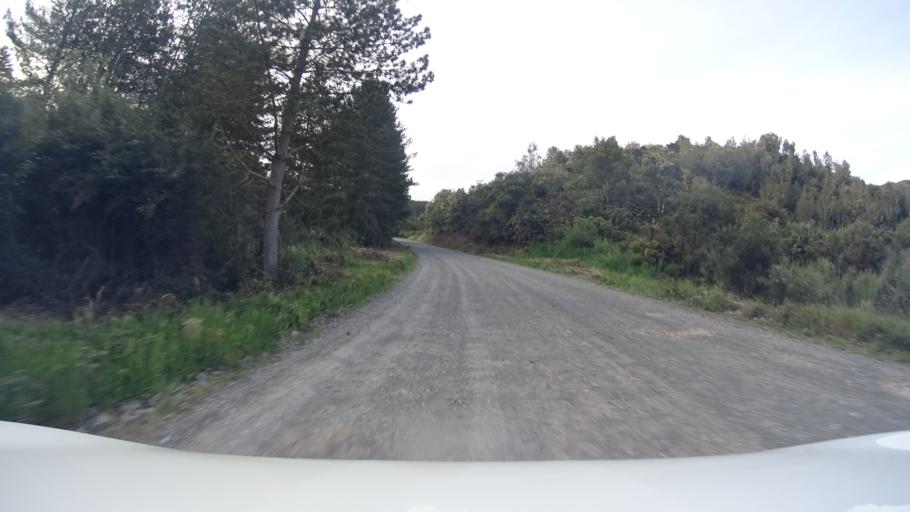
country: NZ
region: Bay of Plenty
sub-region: Rotorua District
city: Rotorua
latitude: -38.3267
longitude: 176.3749
